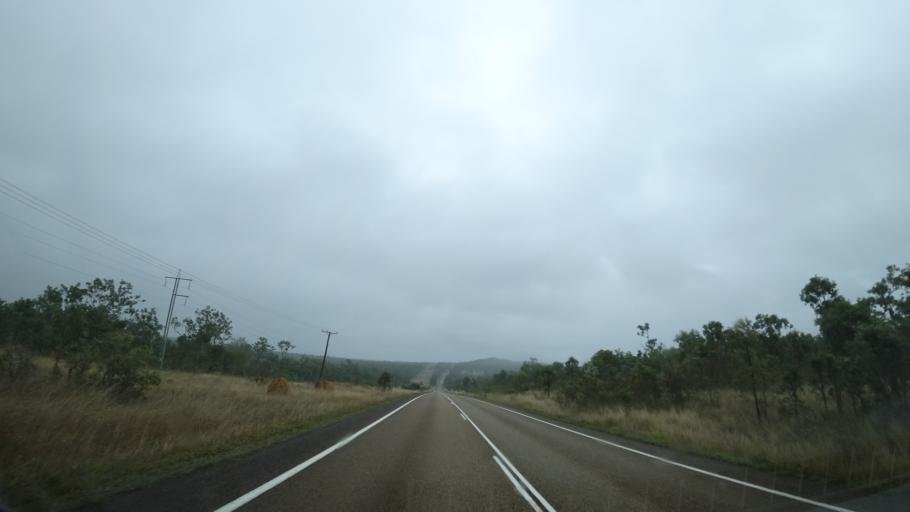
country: AU
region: Queensland
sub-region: Tablelands
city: Ravenshoe
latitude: -17.6985
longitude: 145.2036
